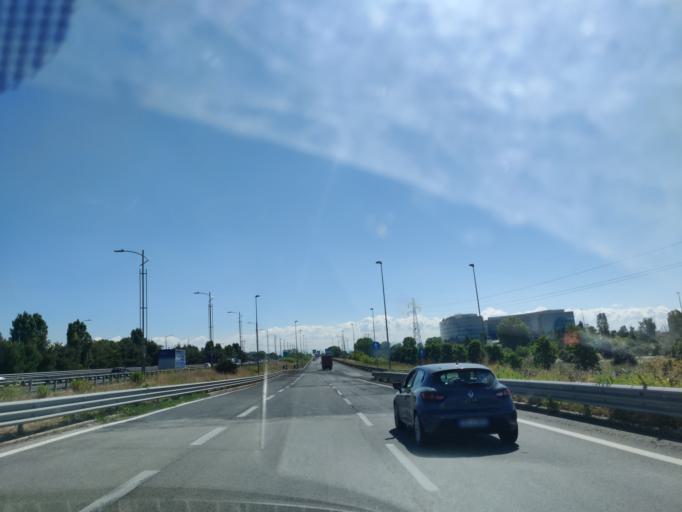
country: IT
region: Latium
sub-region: Citta metropolitana di Roma Capitale
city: Npp 23 (Parco Leonardo)
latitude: 41.8123
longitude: 12.3268
